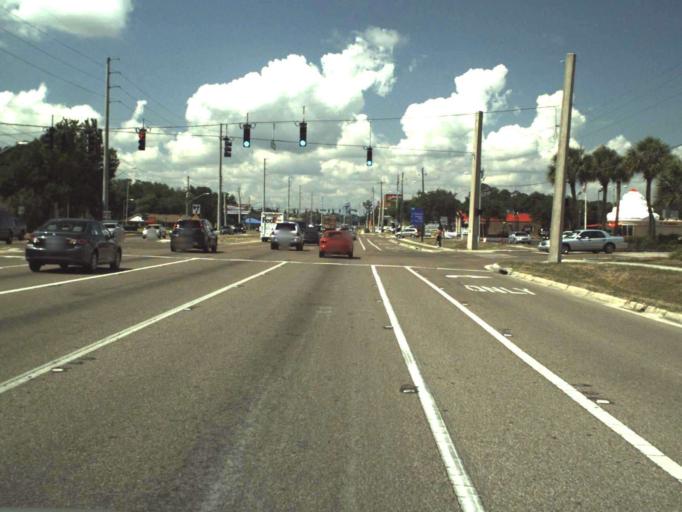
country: US
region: Florida
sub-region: Lake County
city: Tavares
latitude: 28.8183
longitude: -81.7243
